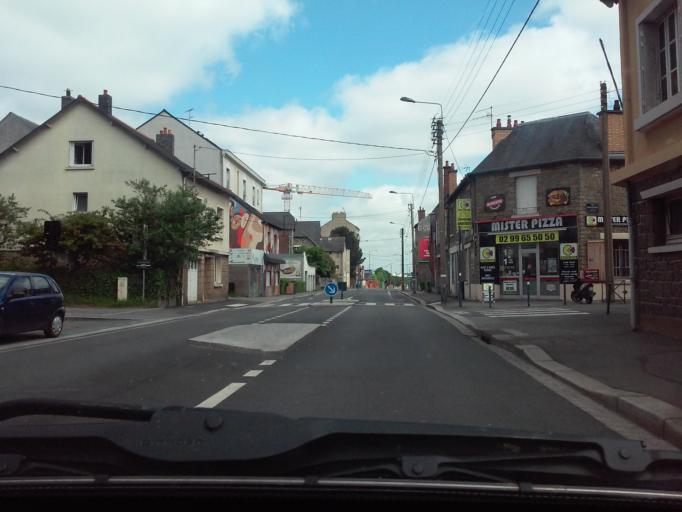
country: FR
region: Brittany
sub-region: Departement d'Ille-et-Vilaine
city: Rennes
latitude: 48.0952
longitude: -1.6900
